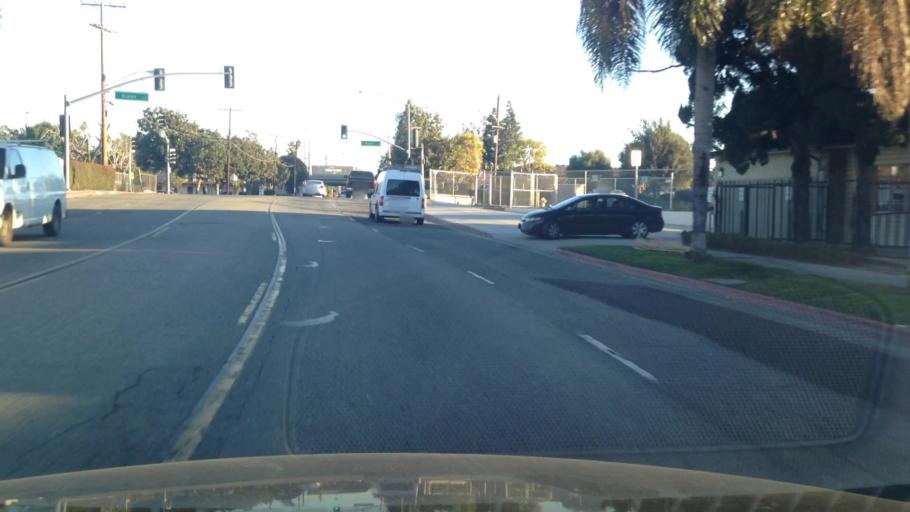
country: US
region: California
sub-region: Riverside County
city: Riverside
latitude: 33.9448
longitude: -117.3961
